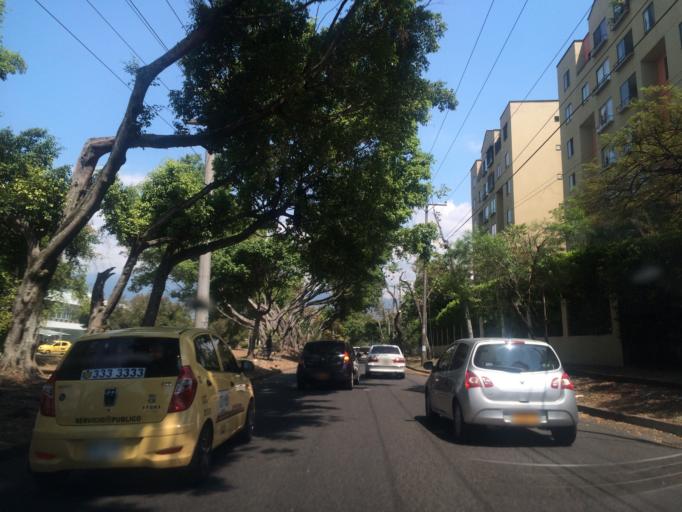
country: CO
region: Valle del Cauca
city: Cali
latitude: 3.4067
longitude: -76.5273
